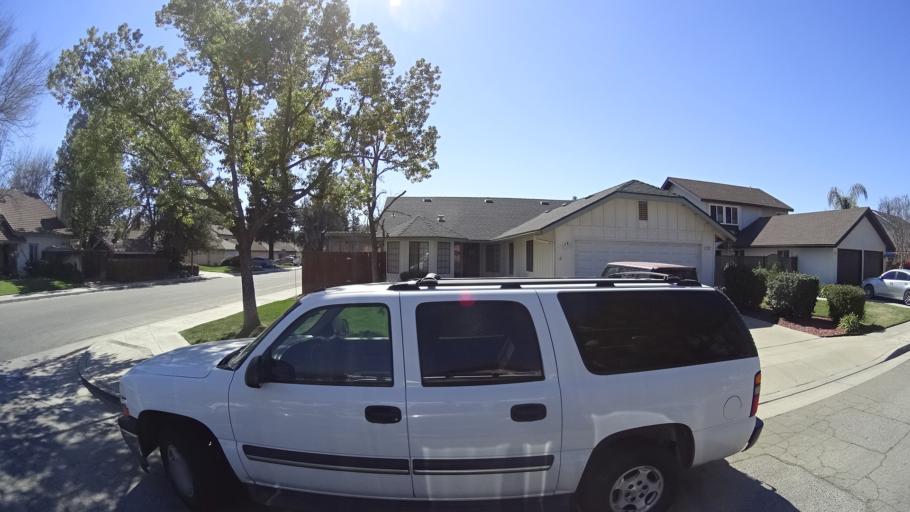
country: US
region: California
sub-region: Fresno County
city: Clovis
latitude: 36.8498
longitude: -119.7647
